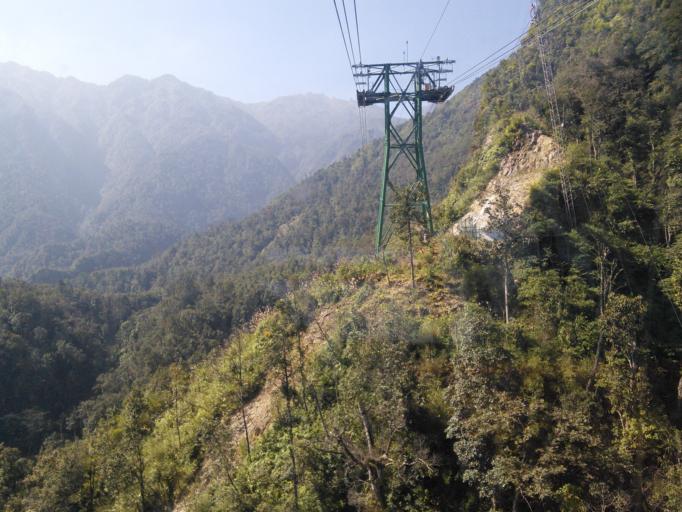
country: VN
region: Lao Cai
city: Sa Pa
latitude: 22.3253
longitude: 103.8050
